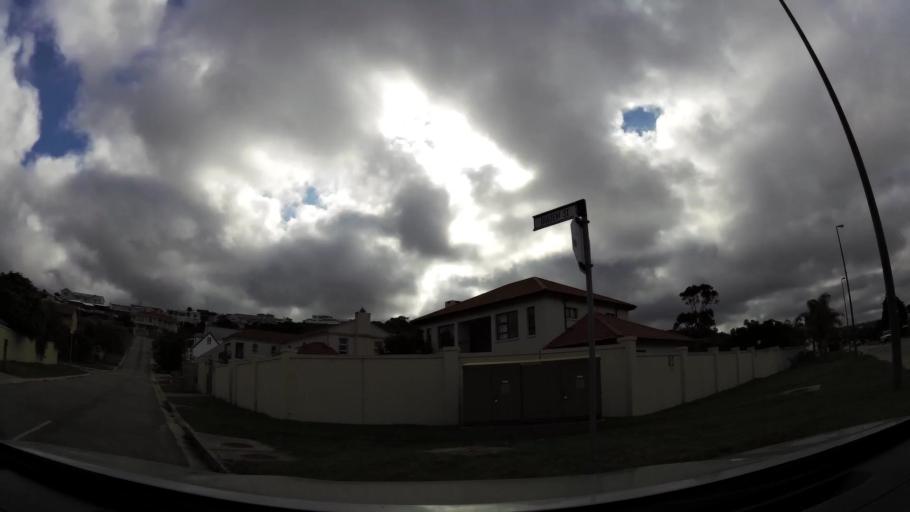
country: ZA
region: Western Cape
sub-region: Eden District Municipality
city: Plettenberg Bay
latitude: -34.0850
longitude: 23.3626
